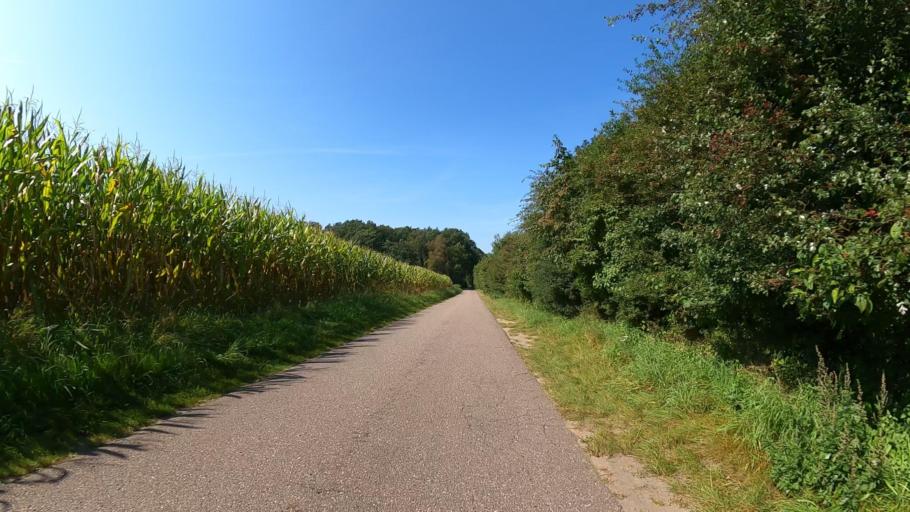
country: DE
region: Schleswig-Holstein
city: Nutzen
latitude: 53.8690
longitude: 9.9053
